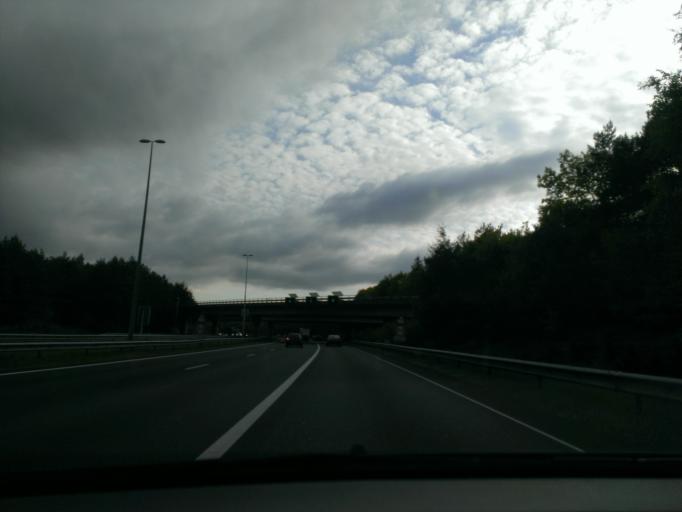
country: NL
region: Gelderland
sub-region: Gemeente Apeldoorn
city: Beekbergen
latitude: 52.1241
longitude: 5.9574
